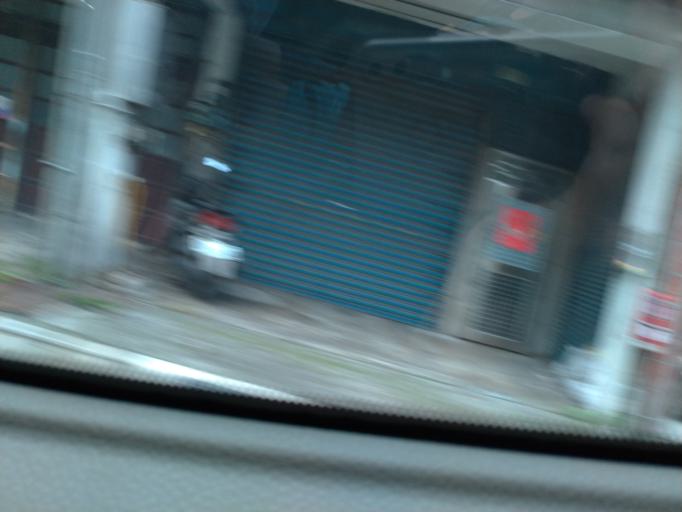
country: TW
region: Taiwan
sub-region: Taoyuan
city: Taoyuan
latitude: 24.9345
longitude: 121.4017
